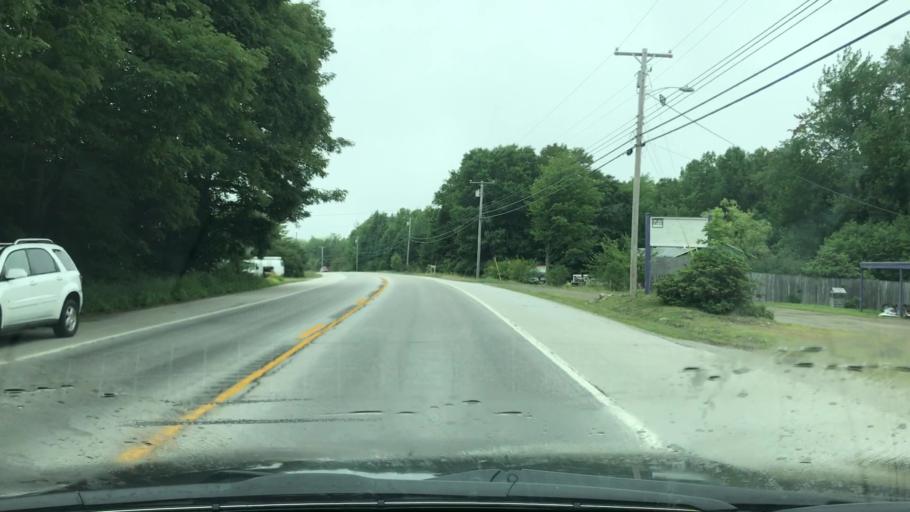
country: US
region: Maine
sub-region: Waldo County
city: Northport
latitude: 44.3294
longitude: -68.9582
